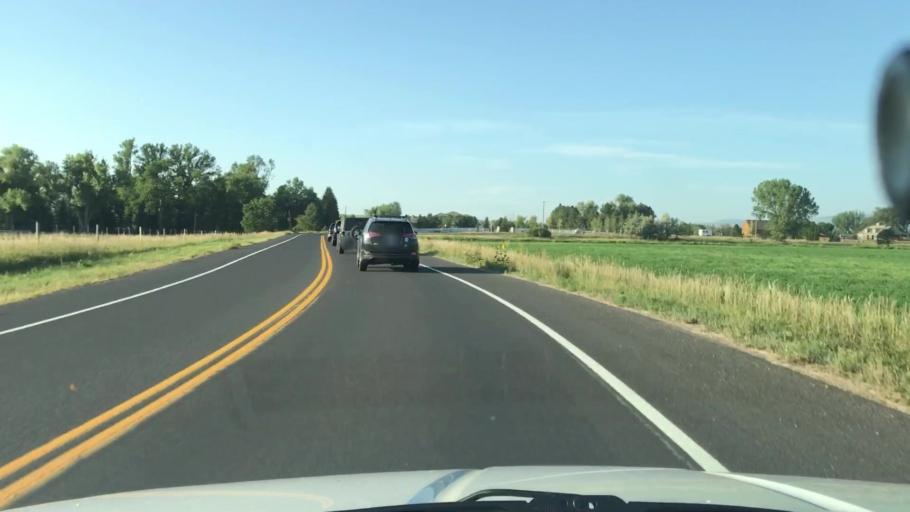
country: US
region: Colorado
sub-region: Boulder County
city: Gunbarrel
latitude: 40.0390
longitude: -105.1550
